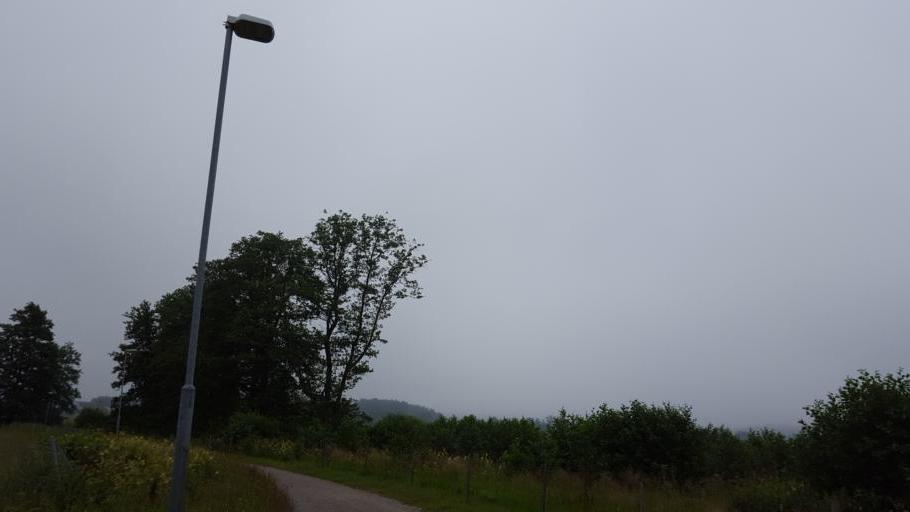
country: SE
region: Stockholm
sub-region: Upplands Vasby Kommun
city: Upplands Vaesby
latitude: 59.5068
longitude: 17.8707
